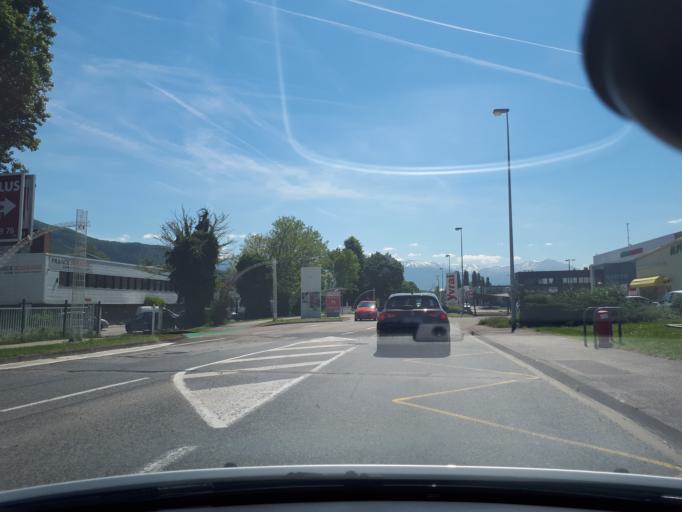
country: FR
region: Rhone-Alpes
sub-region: Departement de l'Isere
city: Saint-Egreve
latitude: 45.2188
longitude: 5.6795
